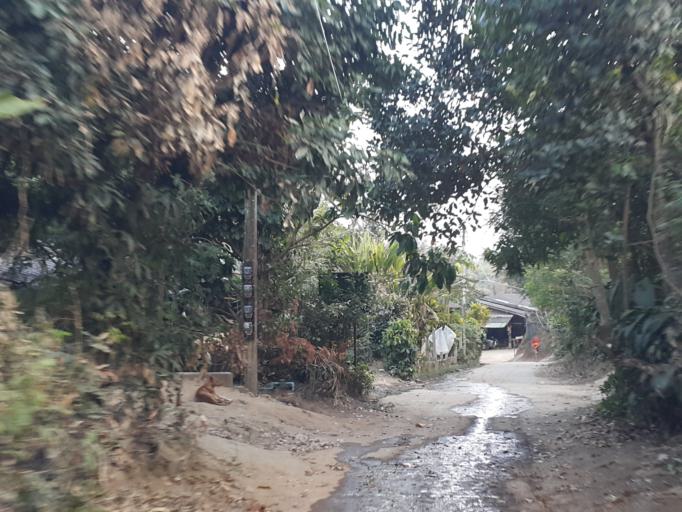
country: TH
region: Chiang Mai
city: Mae Taeng
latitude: 19.1124
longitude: 98.8278
